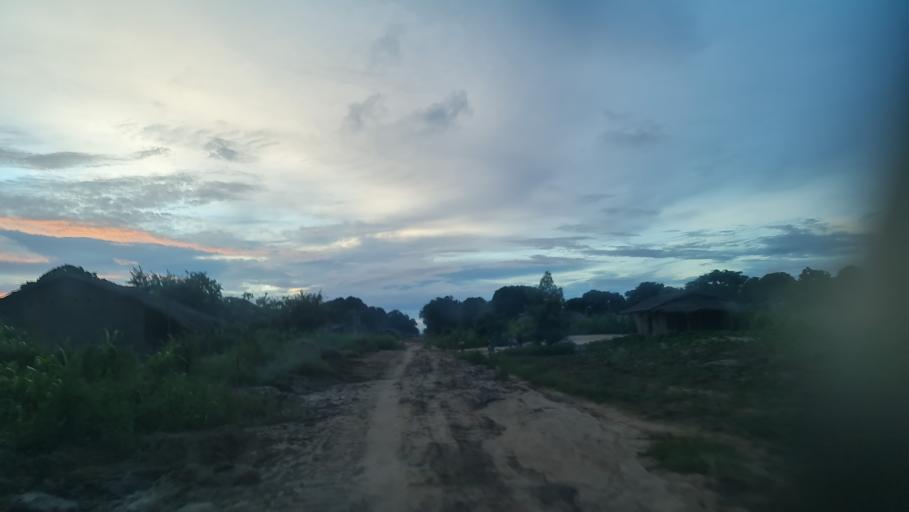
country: MZ
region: Nampula
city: Nampula
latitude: -14.7363
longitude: 39.9236
